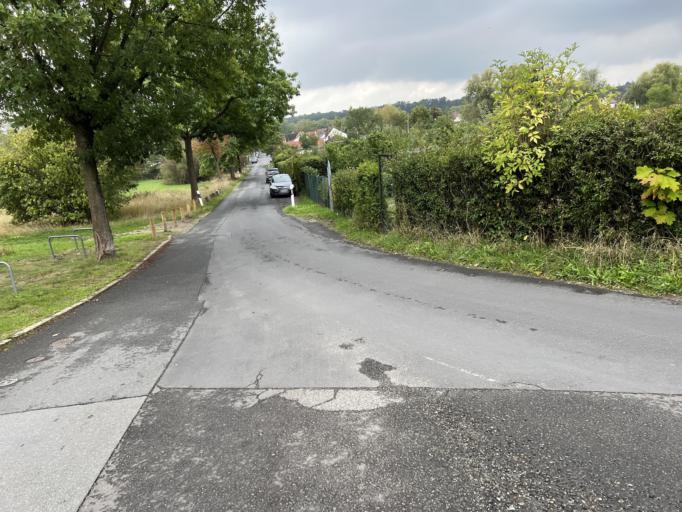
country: DE
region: Hesse
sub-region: Regierungsbezirk Darmstadt
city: Offenbach
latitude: 50.0885
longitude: 8.7817
